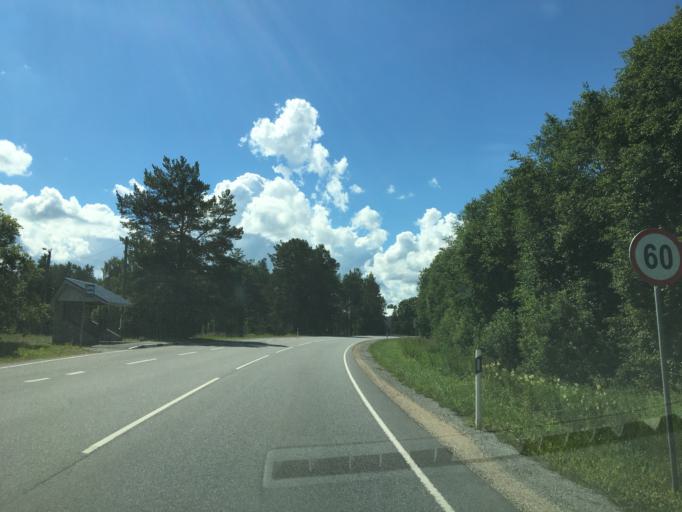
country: EE
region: Harju
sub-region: Nissi vald
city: Riisipere
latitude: 59.2394
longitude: 24.2757
